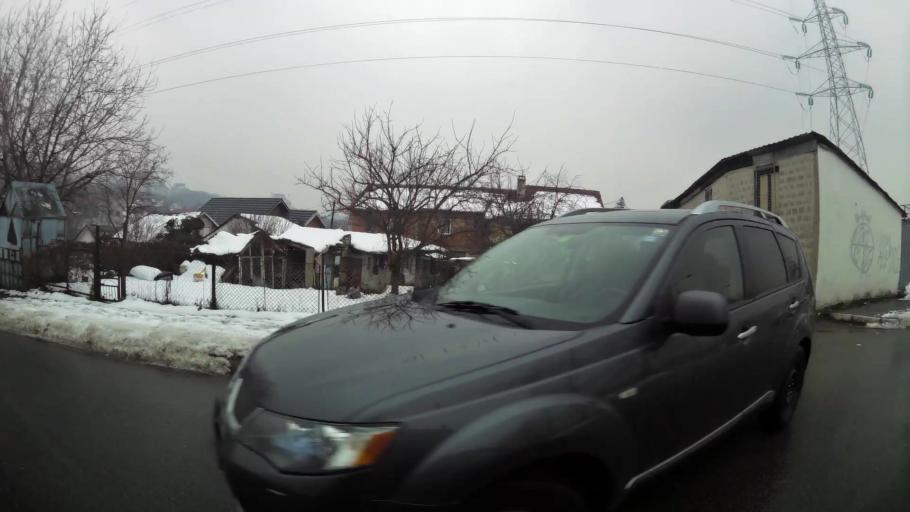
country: RS
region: Central Serbia
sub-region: Belgrade
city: Zvezdara
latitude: 44.7766
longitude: 20.5096
